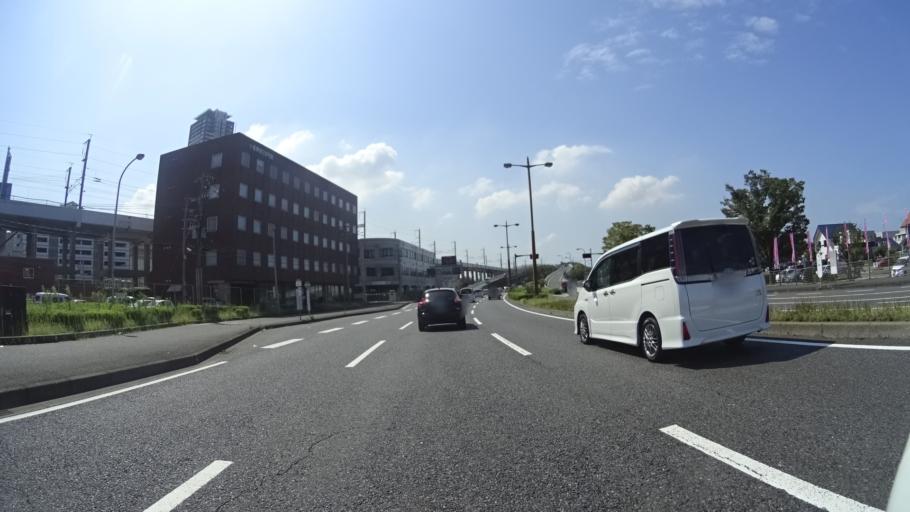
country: JP
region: Fukuoka
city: Kitakyushu
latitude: 33.8891
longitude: 130.8775
